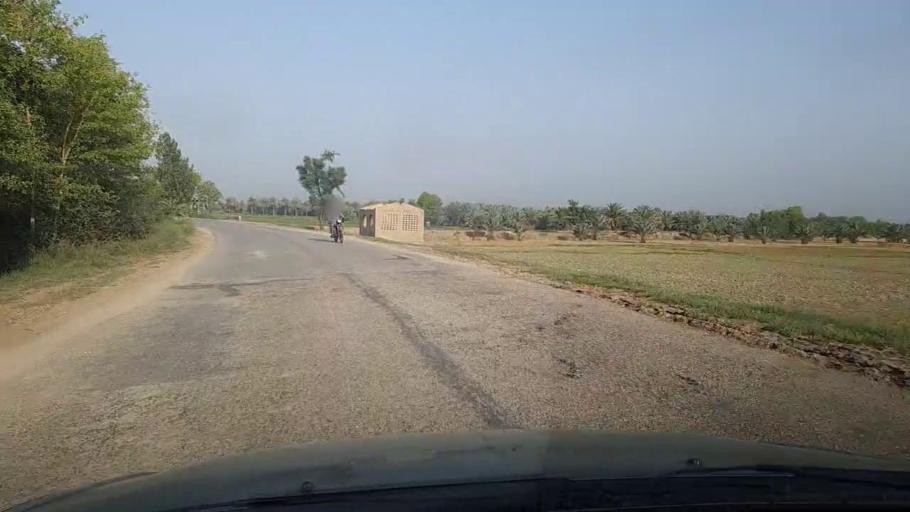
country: PK
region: Sindh
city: Pir jo Goth
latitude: 27.5631
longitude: 68.6578
